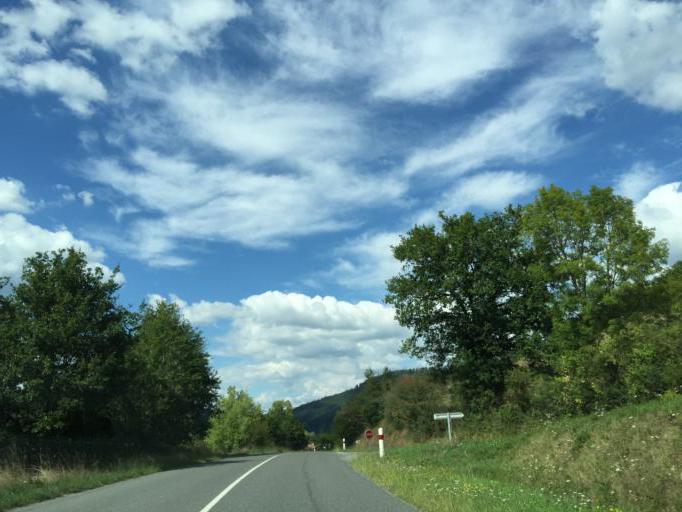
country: FR
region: Midi-Pyrenees
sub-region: Departement de l'Aveyron
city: Saint-Christophe-Vallon
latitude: 44.5374
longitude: 2.4082
